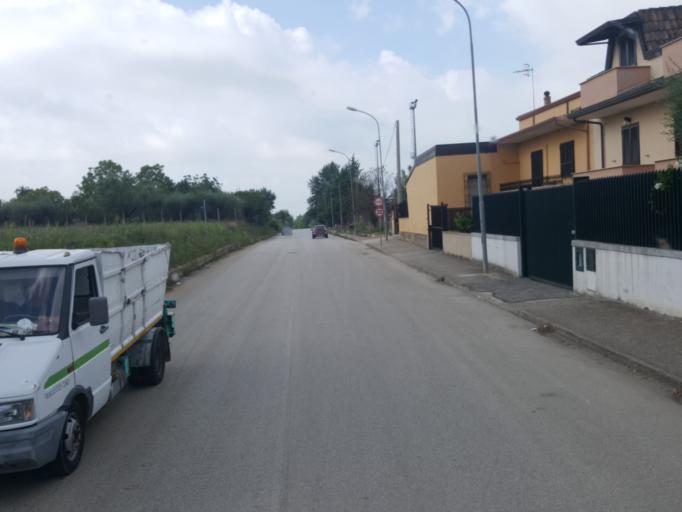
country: IT
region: Campania
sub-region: Provincia di Caserta
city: Pignataro Maggiore
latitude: 41.1885
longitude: 14.1642
